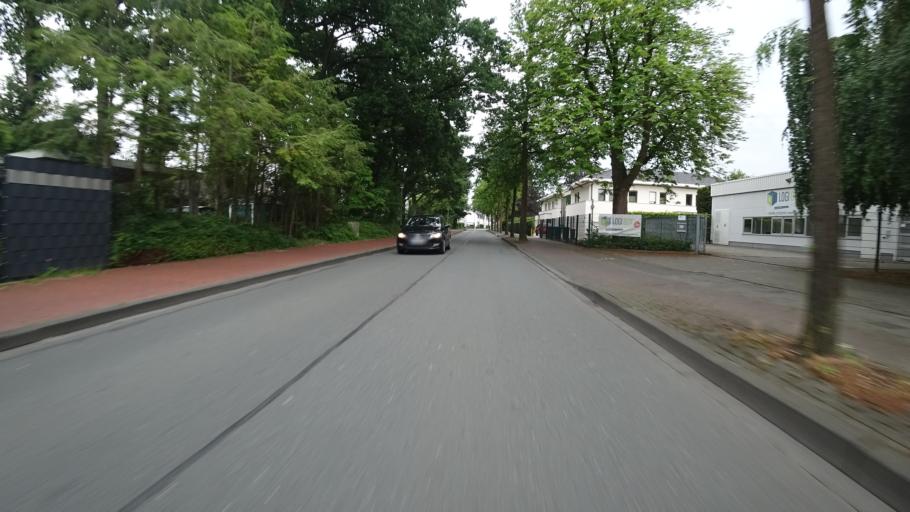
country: DE
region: North Rhine-Westphalia
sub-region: Regierungsbezirk Detmold
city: Guetersloh
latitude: 51.9308
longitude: 8.3840
